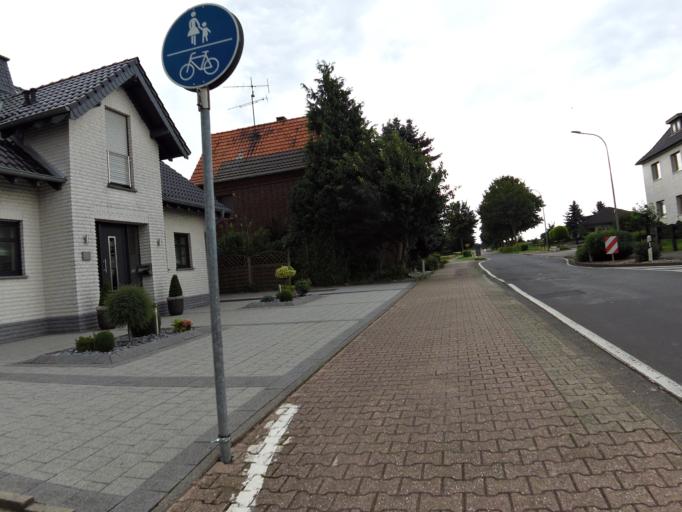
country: DE
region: North Rhine-Westphalia
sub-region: Regierungsbezirk Koln
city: Gangelt
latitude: 51.0031
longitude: 5.9748
